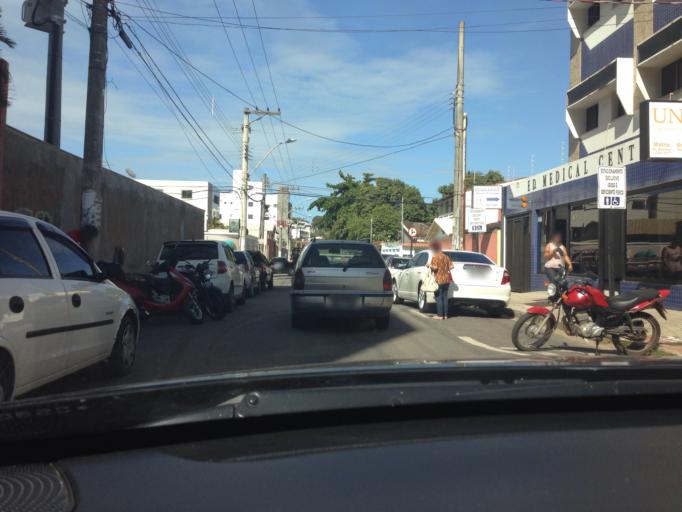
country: BR
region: Espirito Santo
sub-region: Guarapari
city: Guarapari
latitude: -20.6729
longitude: -40.5027
